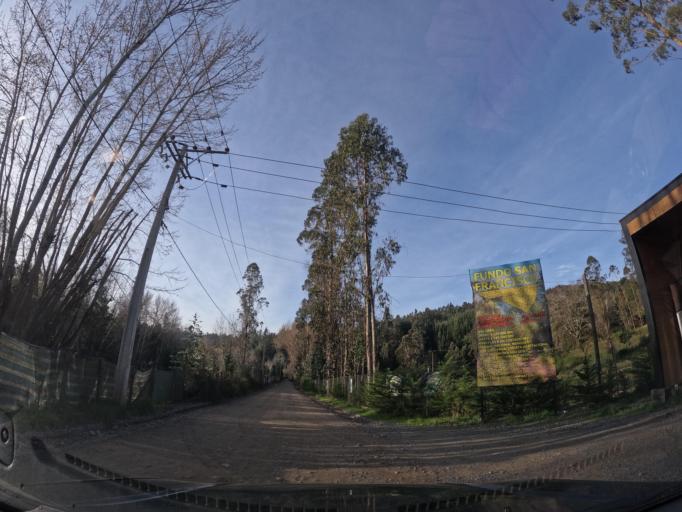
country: CL
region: Biobio
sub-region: Provincia de Concepcion
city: Concepcion
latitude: -36.8628
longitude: -72.9982
